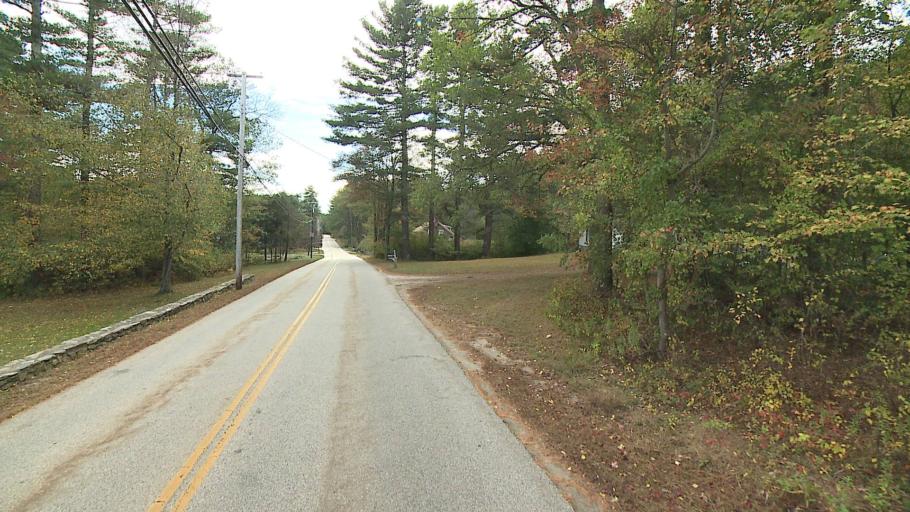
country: US
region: Connecticut
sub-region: Windham County
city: Thompson
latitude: 41.9468
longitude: -71.8195
